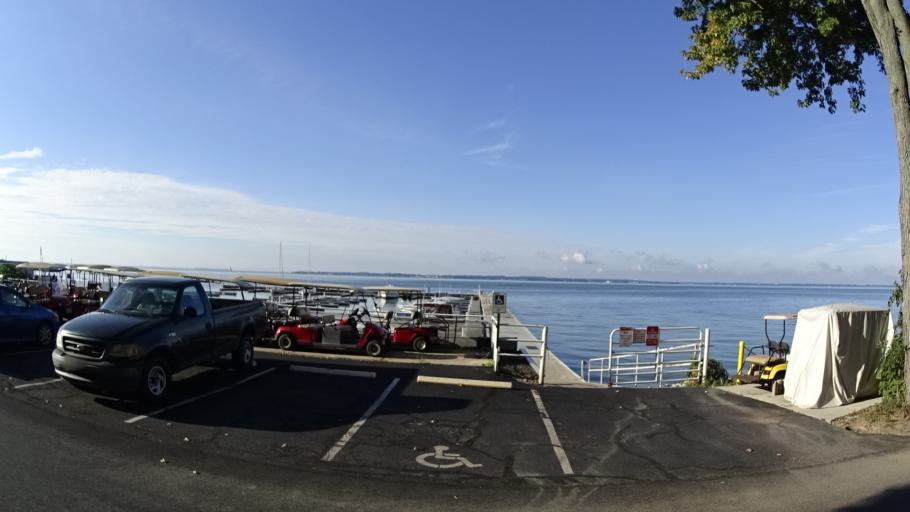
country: US
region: Ohio
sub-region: Erie County
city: Sandusky
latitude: 41.5943
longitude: -82.7126
